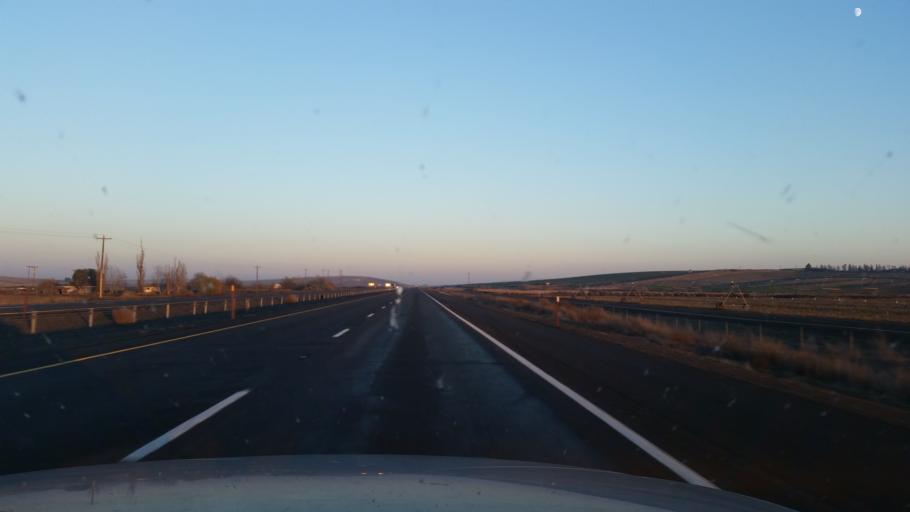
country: US
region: Washington
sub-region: Grant County
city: Warden
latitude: 47.0853
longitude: -119.0283
